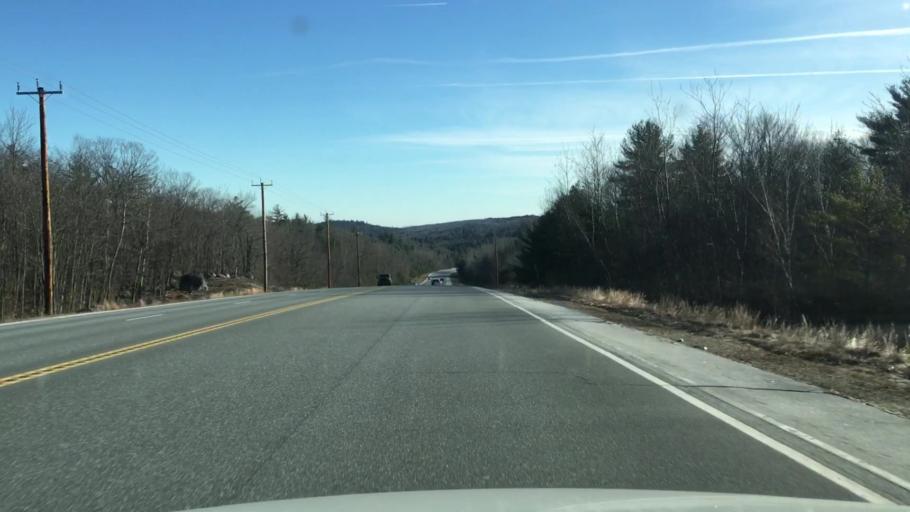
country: US
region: Maine
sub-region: Hancock County
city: Dedham
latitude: 44.6880
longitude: -68.5841
